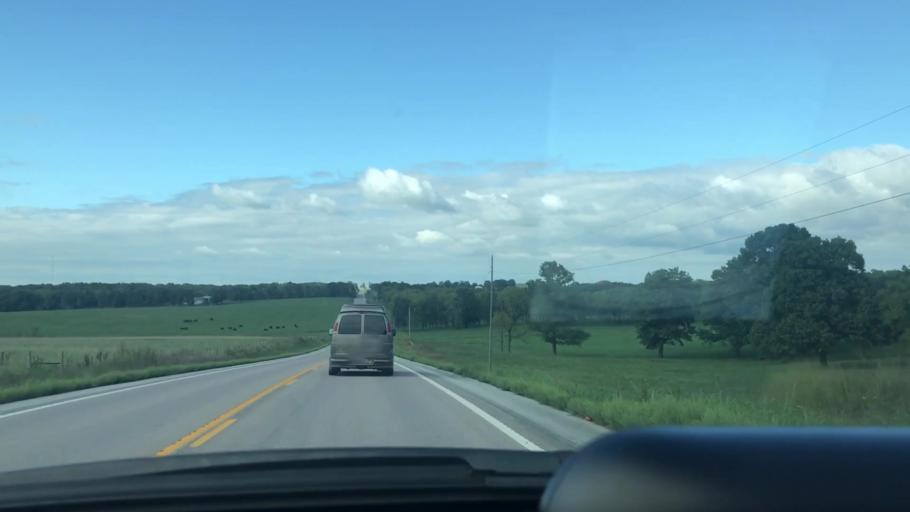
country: US
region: Missouri
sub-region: Hickory County
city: Hermitage
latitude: 37.9663
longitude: -93.2065
